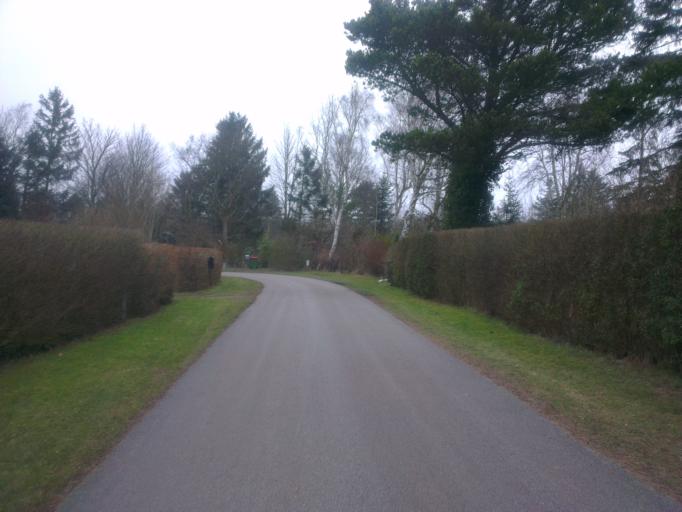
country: DK
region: Capital Region
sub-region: Frederikssund Kommune
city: Jaegerspris
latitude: 55.8329
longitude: 11.9584
